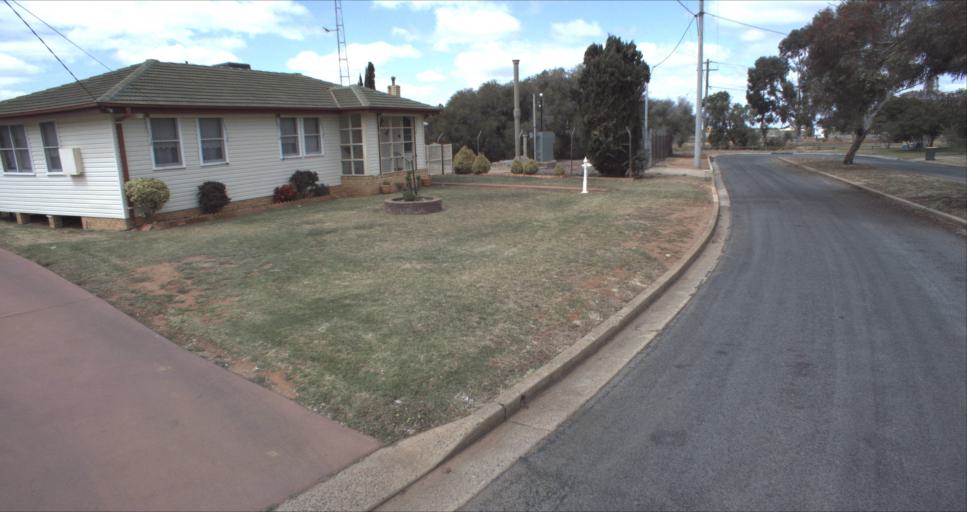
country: AU
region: New South Wales
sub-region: Leeton
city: Leeton
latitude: -34.5672
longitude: 146.3947
